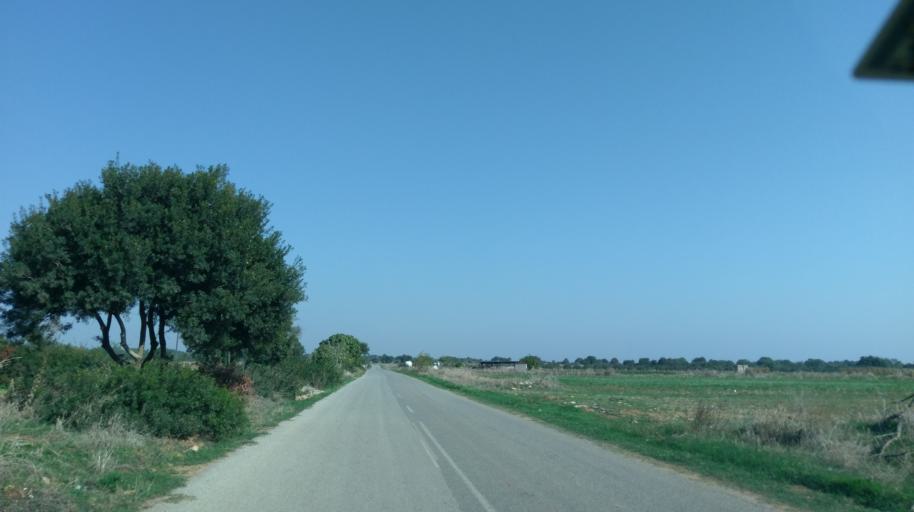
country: CY
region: Ammochostos
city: Leonarisso
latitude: 35.4852
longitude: 34.1989
